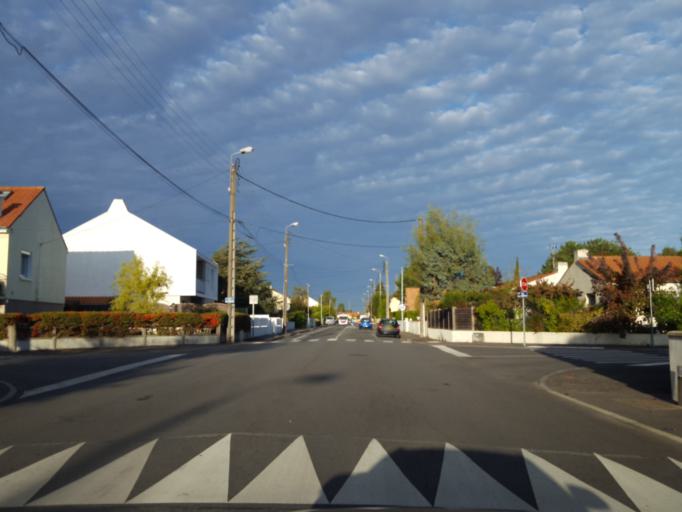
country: FR
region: Pays de la Loire
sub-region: Departement de la Loire-Atlantique
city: Saint-Sebastien-sur-Loire
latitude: 47.1972
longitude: -1.4943
